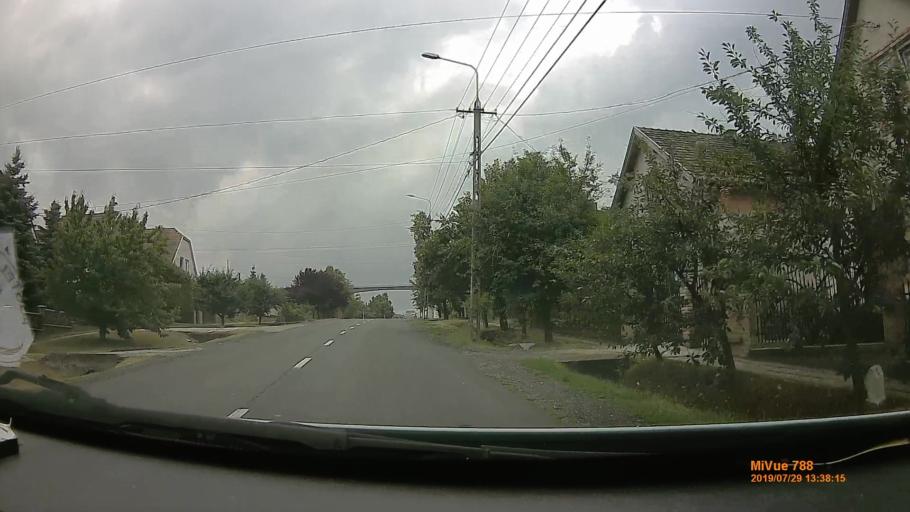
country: HU
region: Somogy
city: Balatonfoldvar
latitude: 46.8234
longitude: 17.9048
